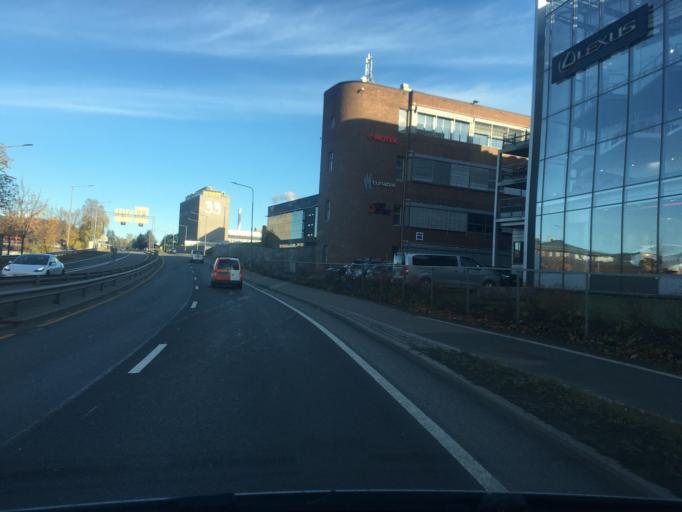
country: NO
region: Oslo
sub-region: Oslo
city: Oslo
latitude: 59.9276
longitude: 10.8131
